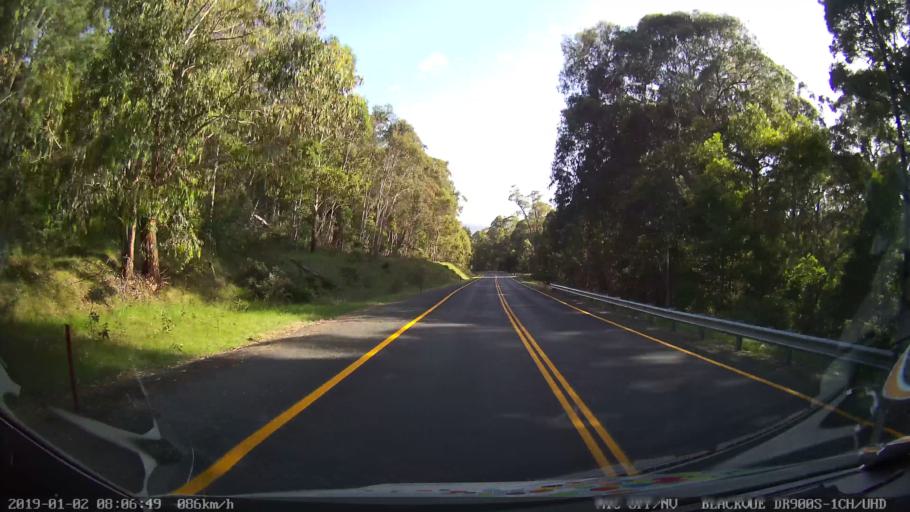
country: AU
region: New South Wales
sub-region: Tumut Shire
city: Tumut
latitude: -35.6356
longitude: 148.3874
